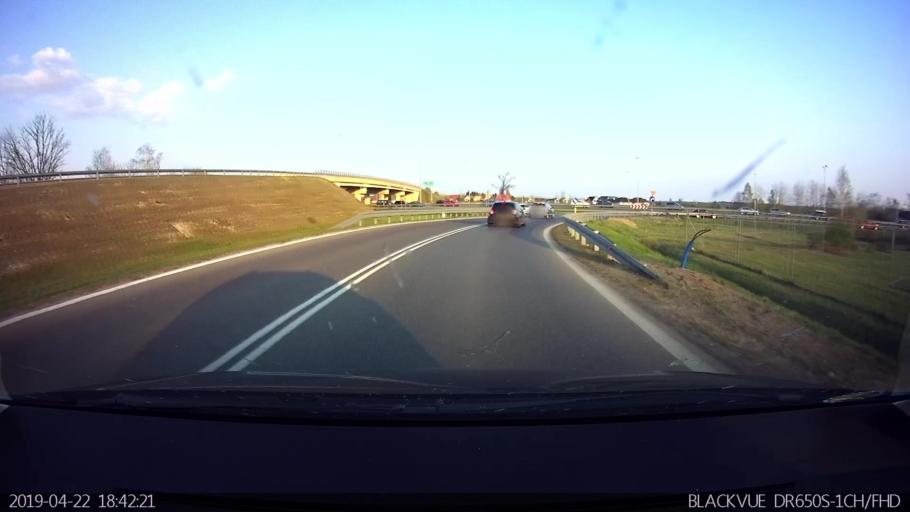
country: PL
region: Masovian Voivodeship
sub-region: Powiat wolominski
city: Dabrowka
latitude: 52.4485
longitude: 21.2613
